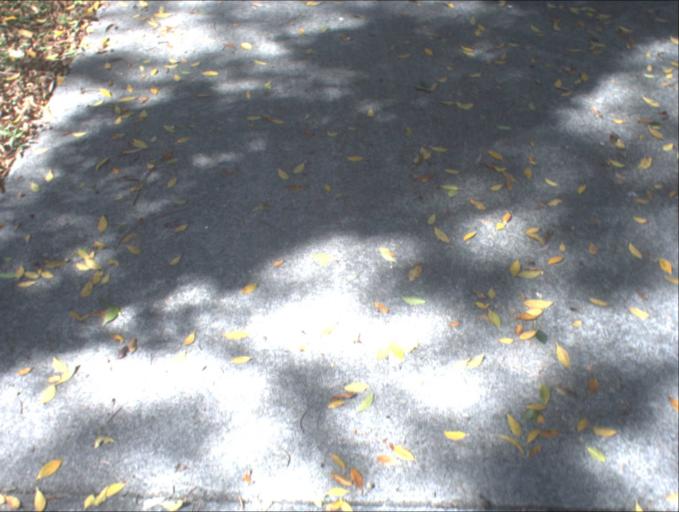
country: AU
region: Queensland
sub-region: Logan
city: Woodridge
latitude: -27.6225
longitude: 153.1077
